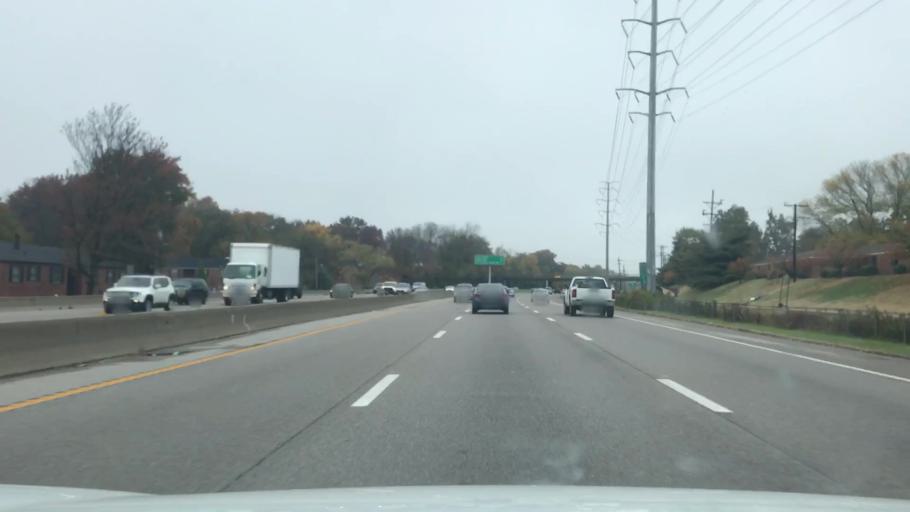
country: US
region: Missouri
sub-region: Saint Louis County
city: Olivette
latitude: 38.6650
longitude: -90.3598
